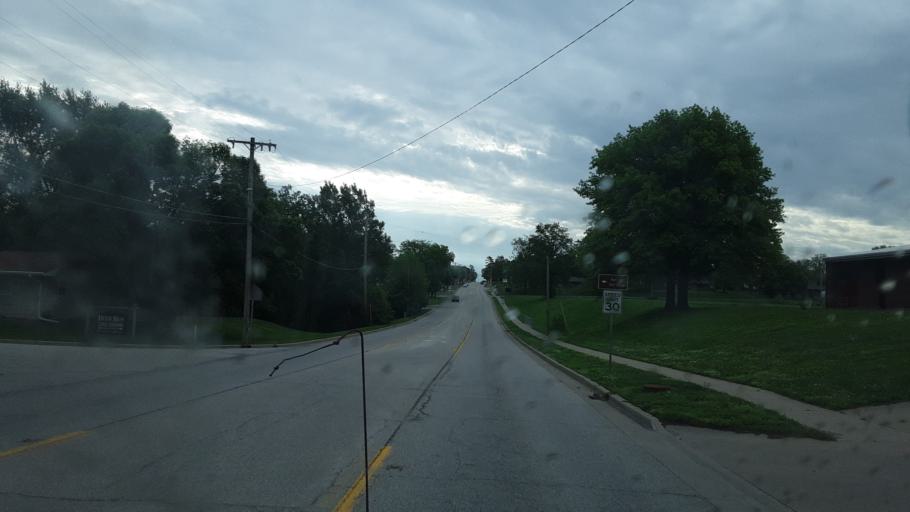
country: US
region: Illinois
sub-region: Hancock County
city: Hamilton
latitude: 40.3965
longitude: -91.3439
